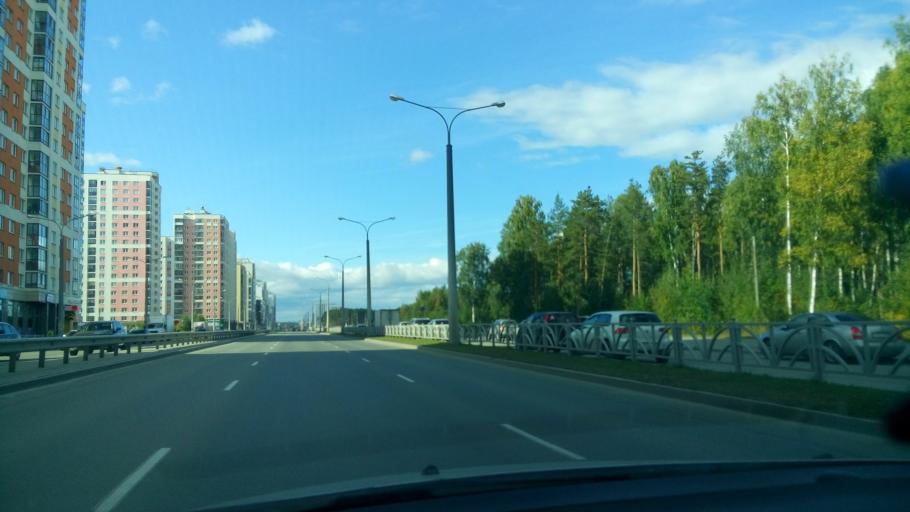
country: RU
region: Sverdlovsk
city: Sovkhoznyy
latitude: 56.7892
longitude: 60.5288
